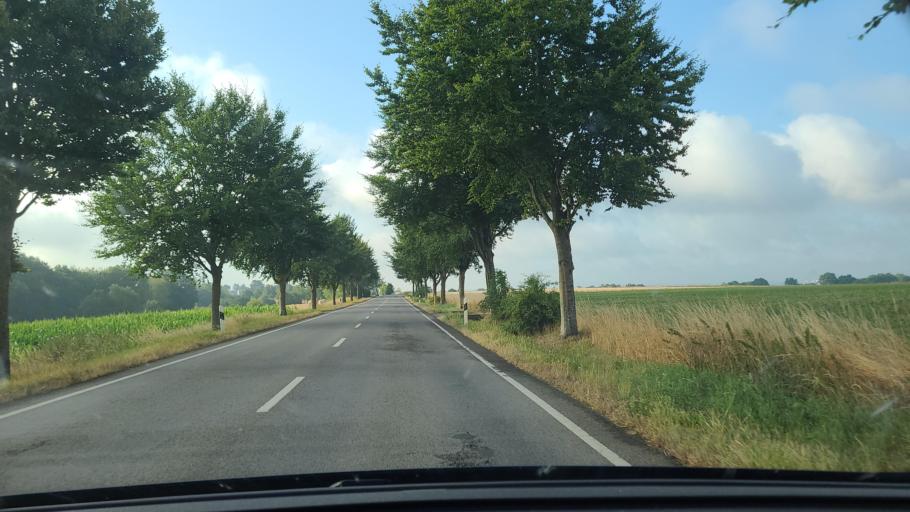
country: LU
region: Luxembourg
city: Schouweiler
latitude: 49.5938
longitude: 5.9590
